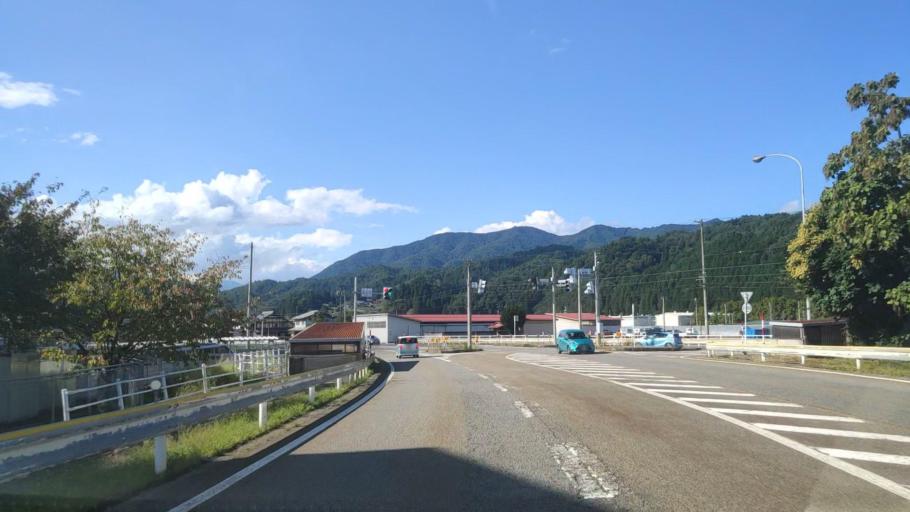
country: JP
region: Gifu
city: Takayama
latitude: 36.2523
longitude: 137.1624
